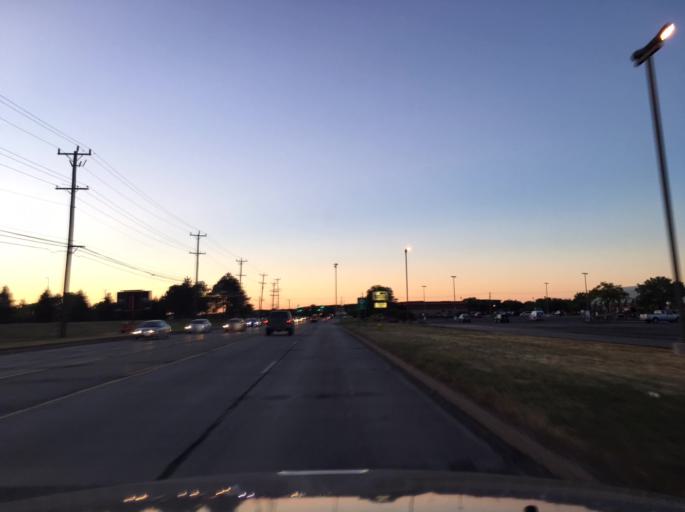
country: US
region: Michigan
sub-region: Macomb County
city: Clinton
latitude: 42.6251
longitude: -82.9532
